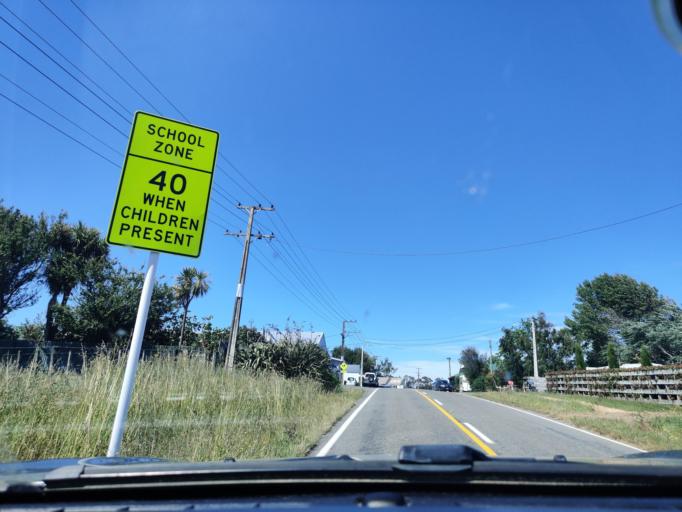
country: NZ
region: Wellington
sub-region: Upper Hutt City
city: Upper Hutt
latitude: -41.3515
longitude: 175.2060
